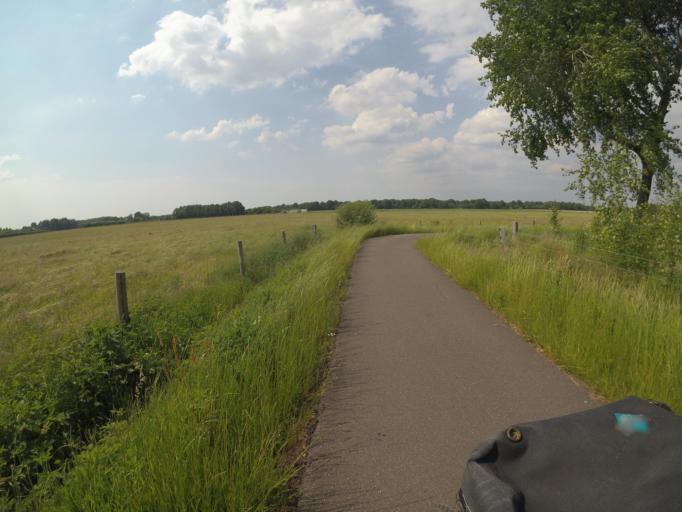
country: NL
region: Drenthe
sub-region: Gemeente Assen
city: Assen
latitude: 52.9675
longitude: 6.5032
